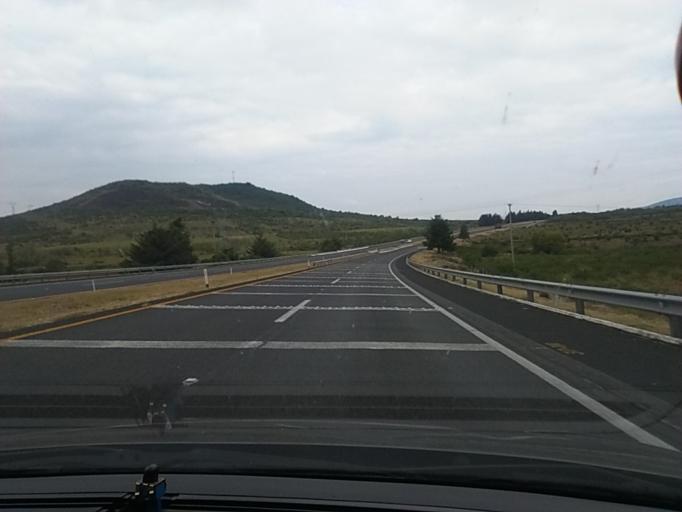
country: MX
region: Michoacan
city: Panindicuaro de la Reforma
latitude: 19.9954
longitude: -101.8147
